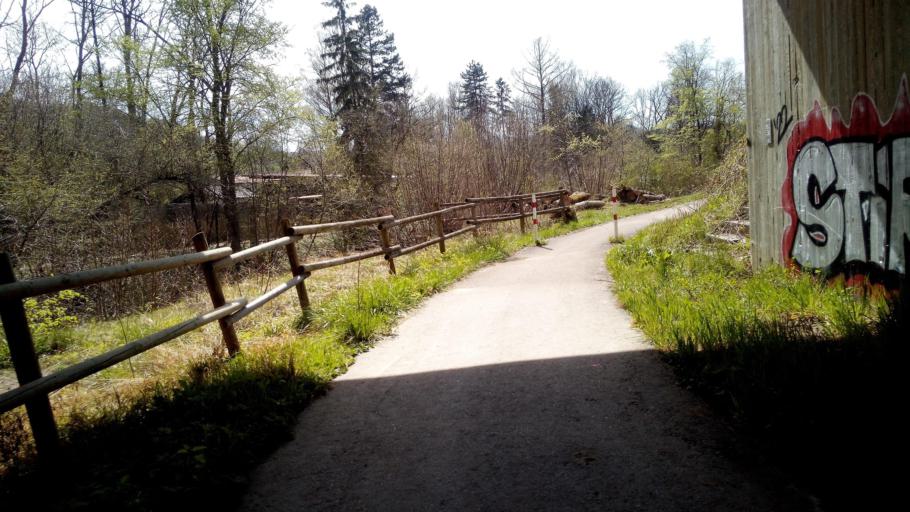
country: DE
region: Baden-Wuerttemberg
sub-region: Regierungsbezirk Stuttgart
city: Donzdorf
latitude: 48.6977
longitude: 9.8173
